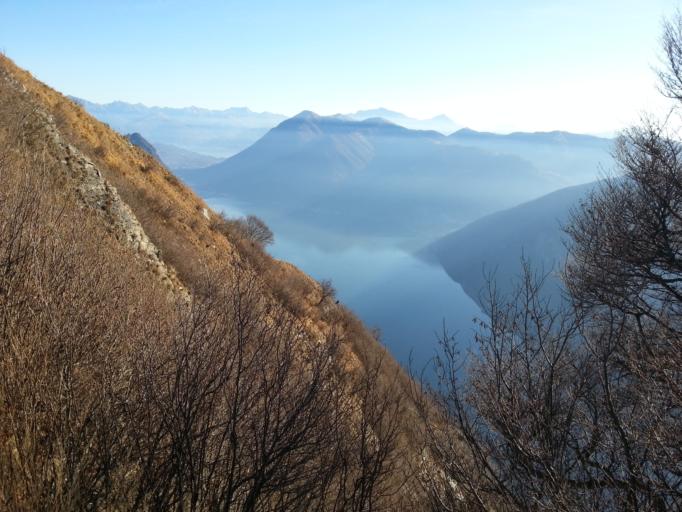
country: CH
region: Ticino
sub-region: Lugano District
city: Cadro
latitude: 46.0268
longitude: 9.0091
